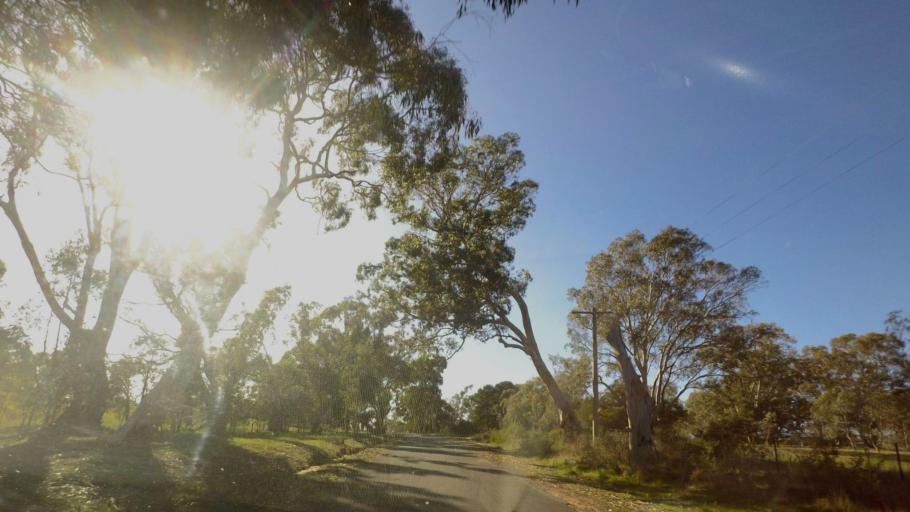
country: AU
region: Victoria
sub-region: Mount Alexander
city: Castlemaine
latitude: -37.1064
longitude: 144.4208
